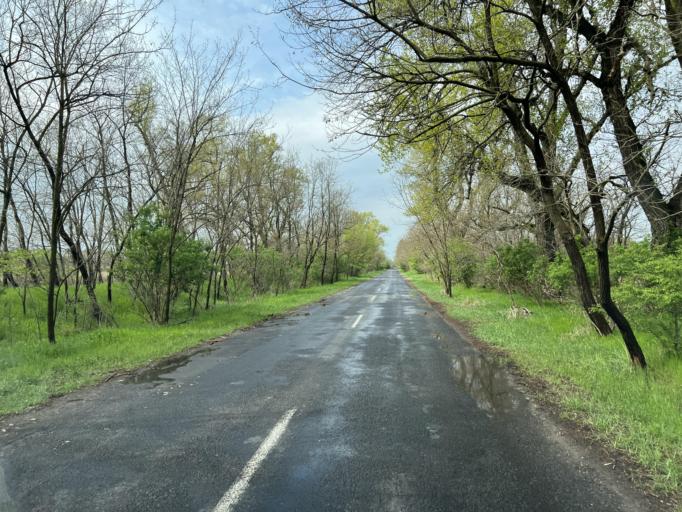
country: HU
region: Pest
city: Danszentmiklos
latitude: 47.1681
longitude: 19.5167
